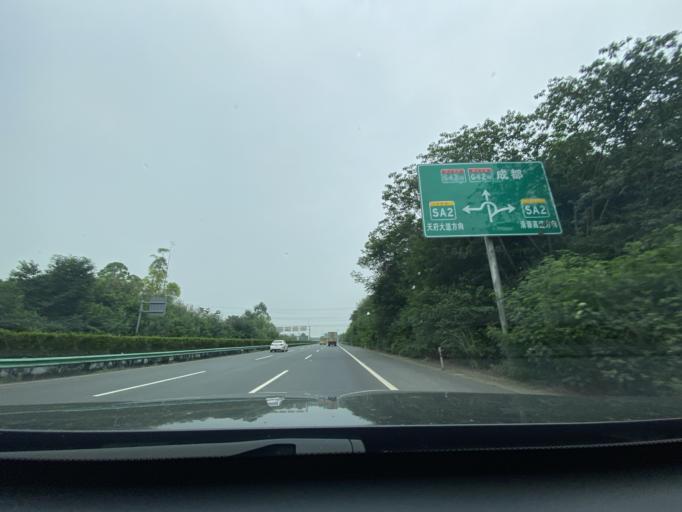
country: CN
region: Sichuan
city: Longquan
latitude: 30.3317
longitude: 104.1198
